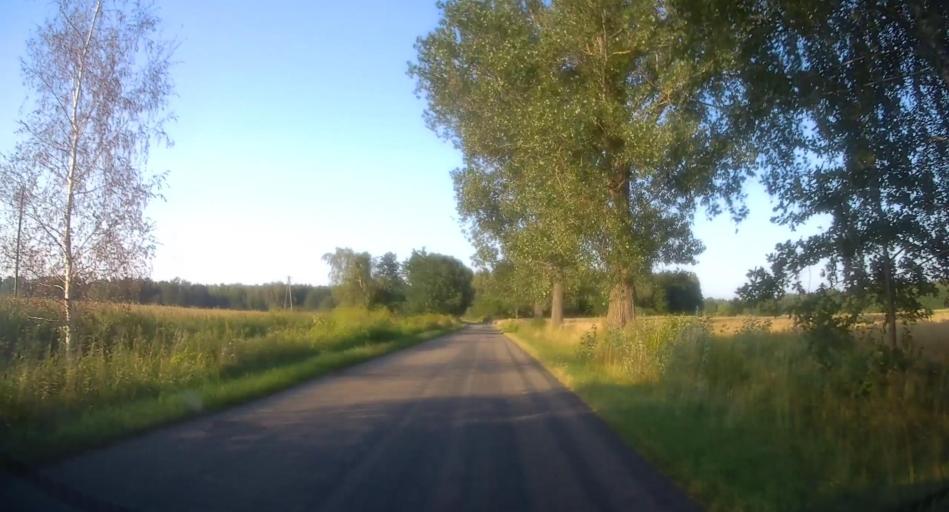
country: PL
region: Lodz Voivodeship
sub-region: Powiat skierniewicki
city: Kaweczyn Nowy
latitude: 51.8874
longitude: 20.2863
